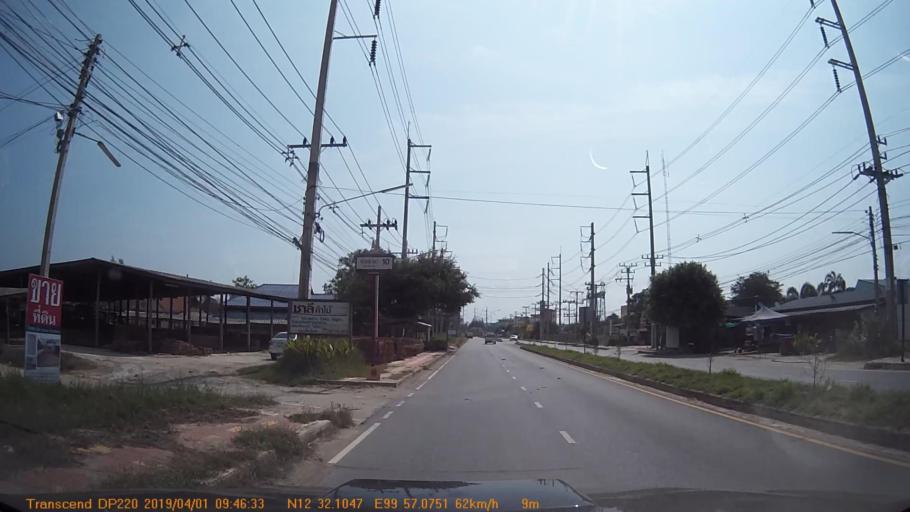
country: TH
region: Prachuap Khiri Khan
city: Hua Hin
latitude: 12.5351
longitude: 99.9515
